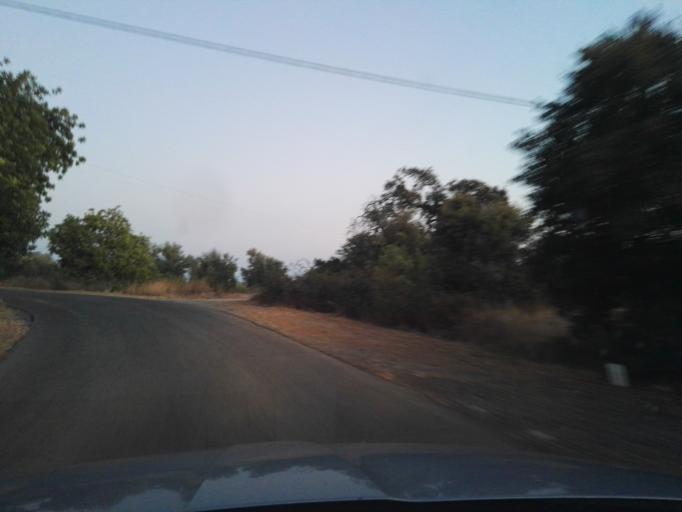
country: PT
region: Faro
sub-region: Sao Bras de Alportel
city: Sao Bras de Alportel
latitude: 37.1560
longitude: -7.9411
